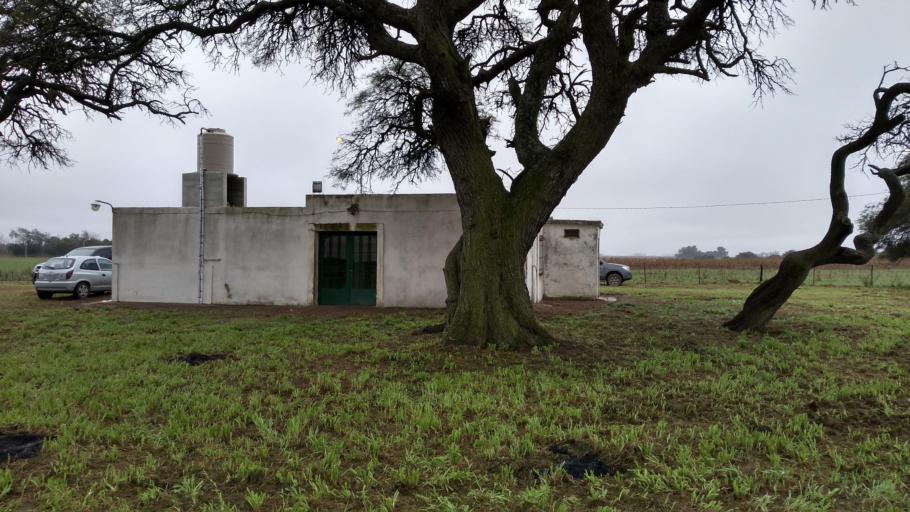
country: AR
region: Cordoba
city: Tio Pujio
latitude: -32.3174
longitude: -63.5129
